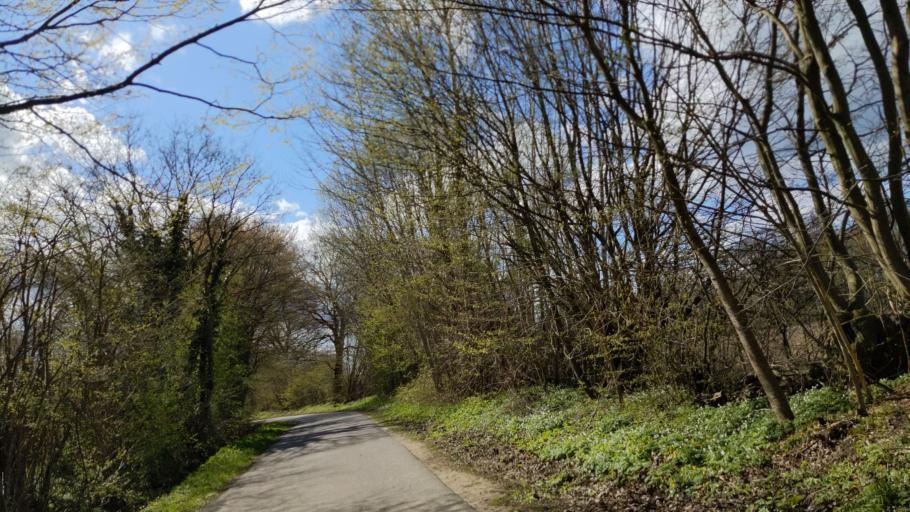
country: DE
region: Mecklenburg-Vorpommern
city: Selmsdorf
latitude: 53.8842
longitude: 10.8727
